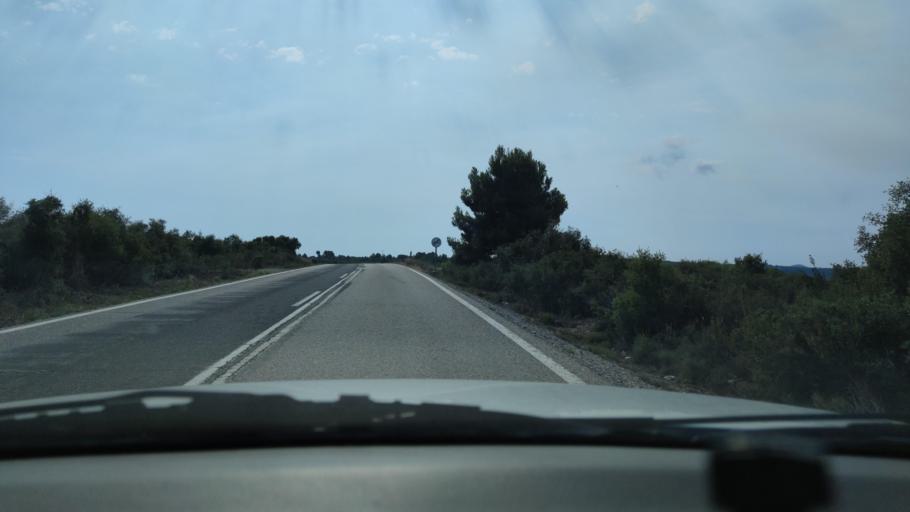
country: ES
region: Catalonia
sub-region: Provincia de Lleida
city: Arbeca
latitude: 41.5027
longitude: 0.9410
